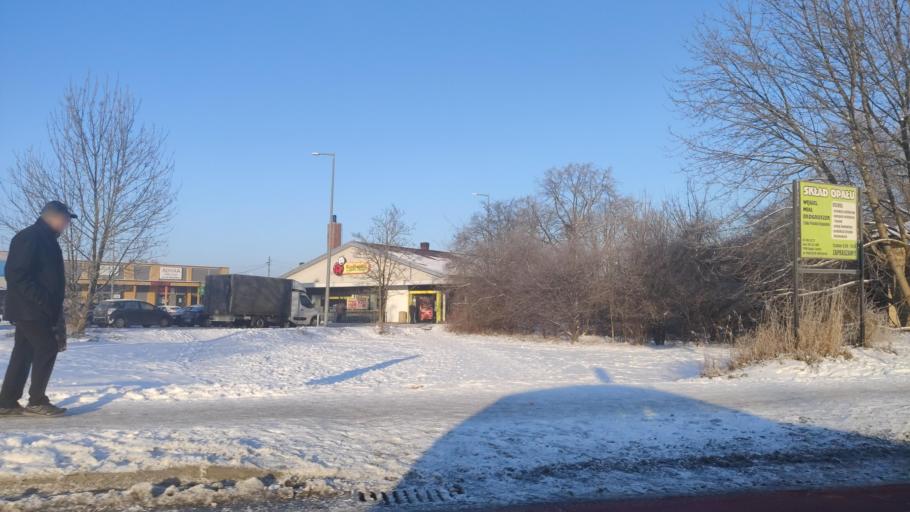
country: PL
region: Kujawsko-Pomorskie
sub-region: Powiat zninski
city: Barcin
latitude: 52.8579
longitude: 17.9420
